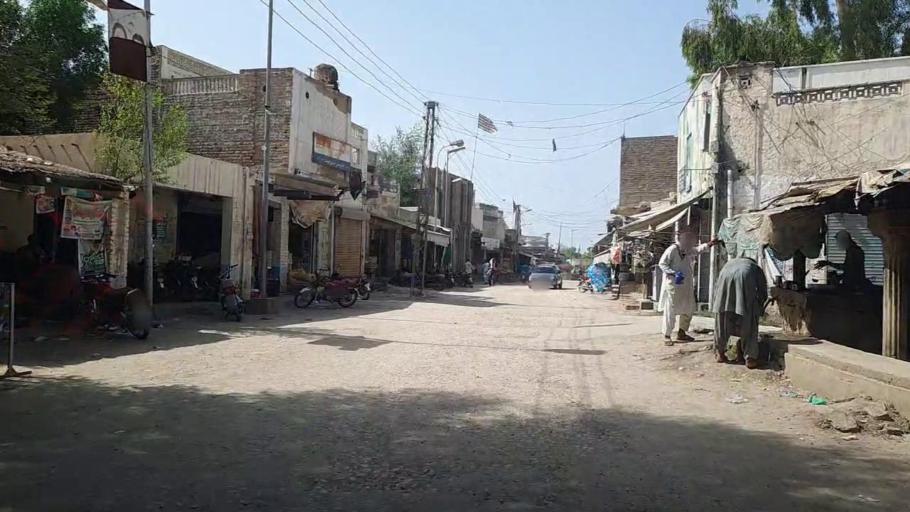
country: PK
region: Sindh
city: Karaundi
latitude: 26.8669
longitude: 68.3638
